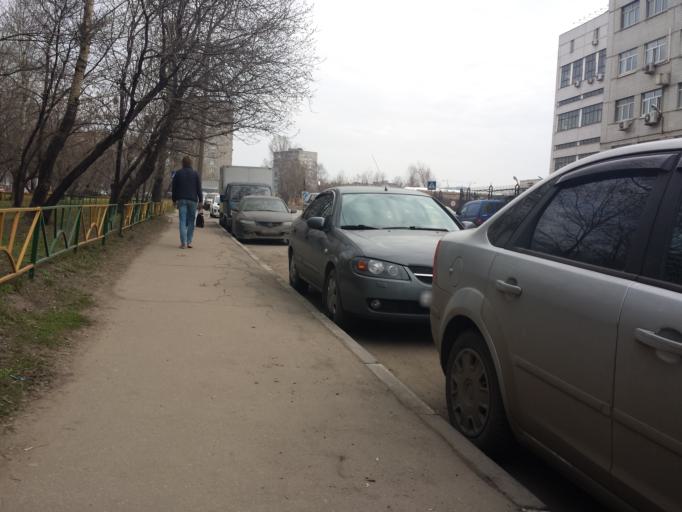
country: RU
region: Moskovskaya
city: Novogireyevo
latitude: 55.7472
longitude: 37.8277
